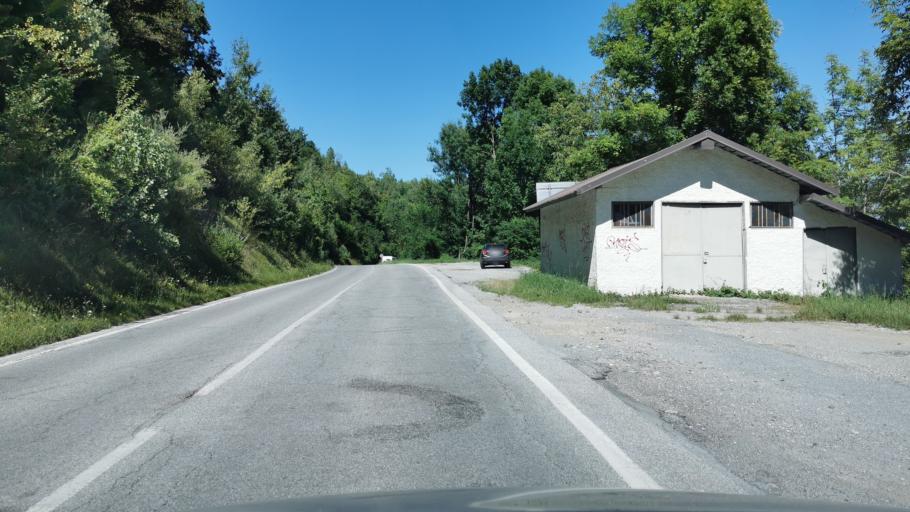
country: IT
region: Piedmont
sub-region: Provincia di Cuneo
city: Roccavione
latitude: 44.3129
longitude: 7.4589
